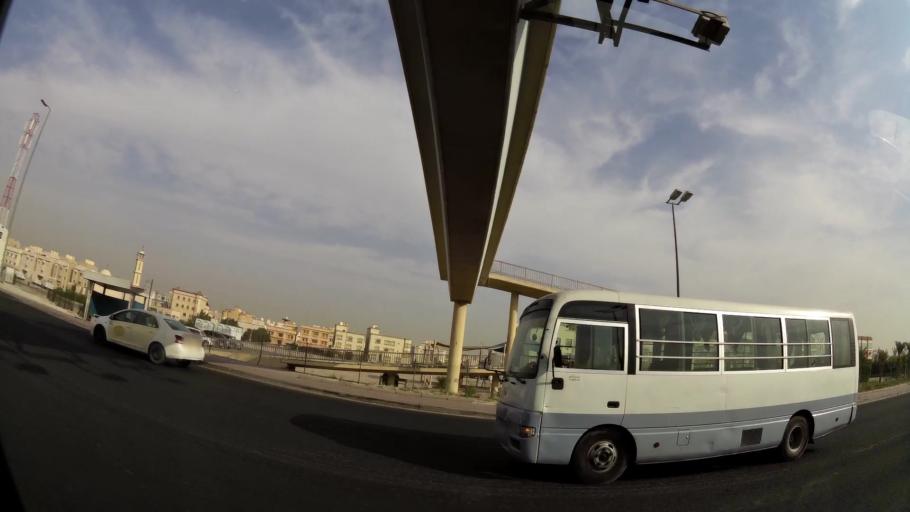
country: KW
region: Al Farwaniyah
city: Al Farwaniyah
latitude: 29.2666
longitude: 47.9467
